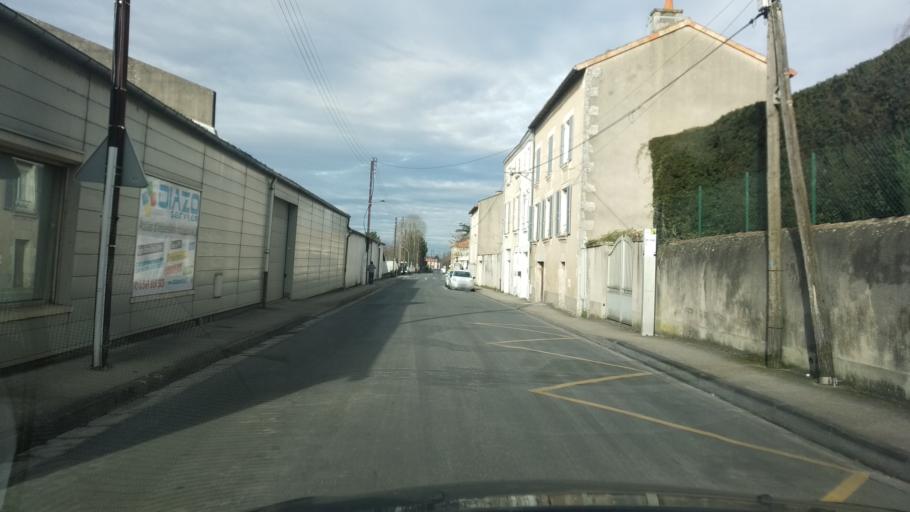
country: FR
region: Poitou-Charentes
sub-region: Departement de la Vienne
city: Poitiers
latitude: 46.5960
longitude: 0.3417
